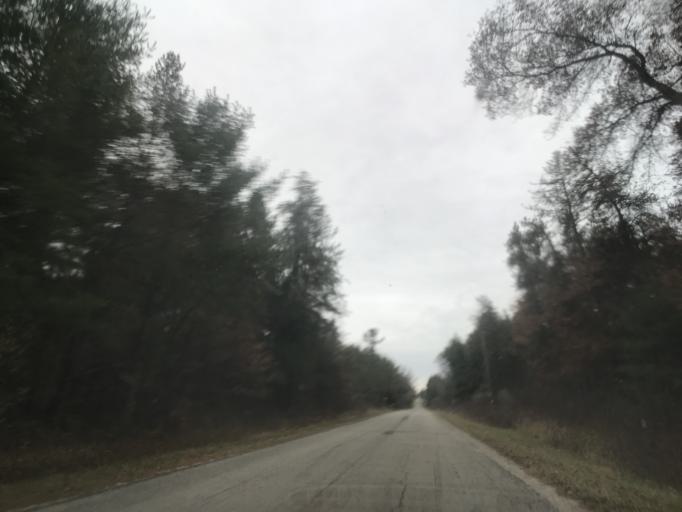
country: US
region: Wisconsin
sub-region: Oconto County
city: Gillett
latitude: 45.2861
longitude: -88.2570
